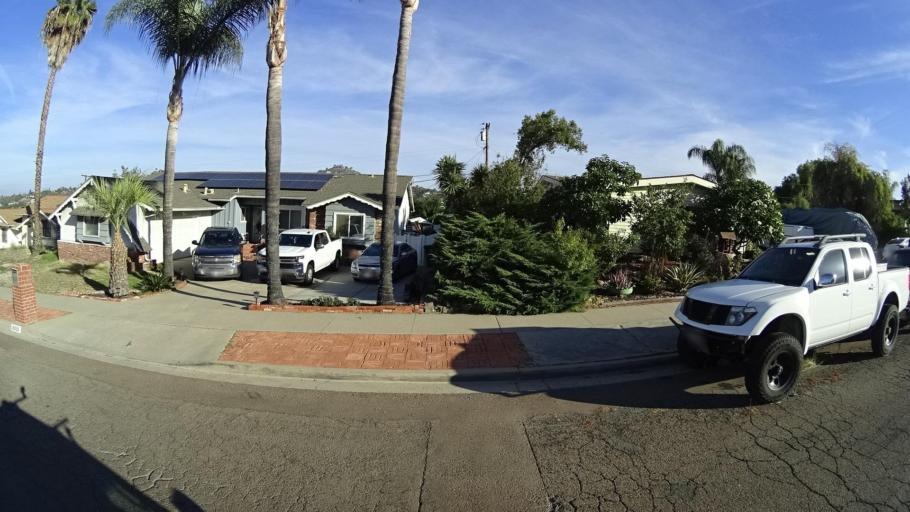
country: US
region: California
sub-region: San Diego County
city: Spring Valley
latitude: 32.7429
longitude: -116.9770
